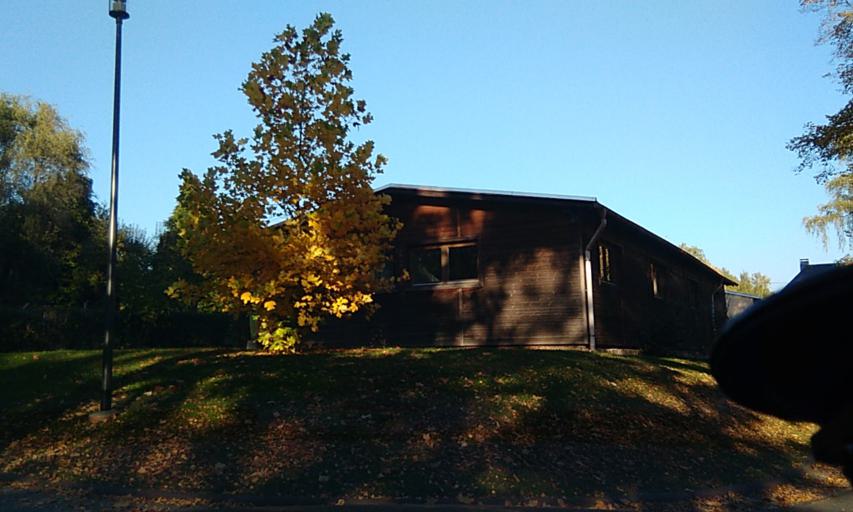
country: DE
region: Saxony
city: Wittgensdorf
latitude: 50.8438
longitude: 12.8787
